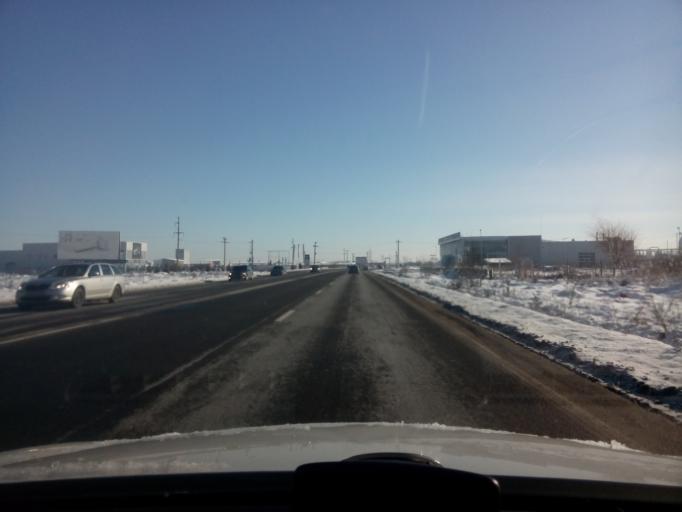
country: RO
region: Arges
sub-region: Comuna Bradu
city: Geamana
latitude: 44.8231
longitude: 24.9243
